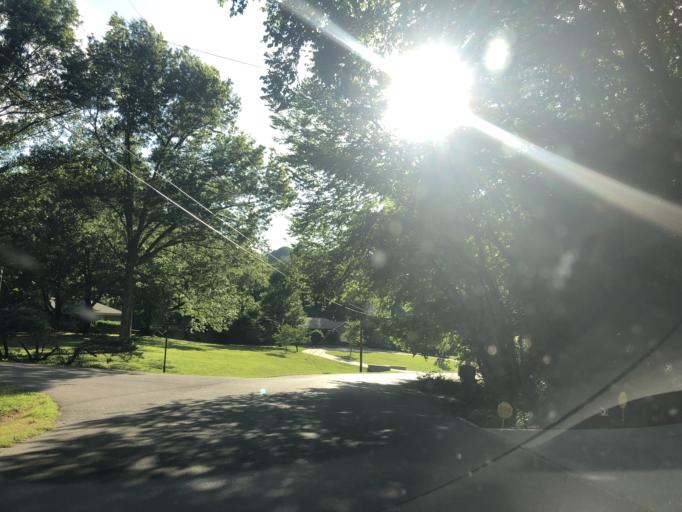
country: US
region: Tennessee
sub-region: Davidson County
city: Forest Hills
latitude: 36.0693
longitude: -86.8251
